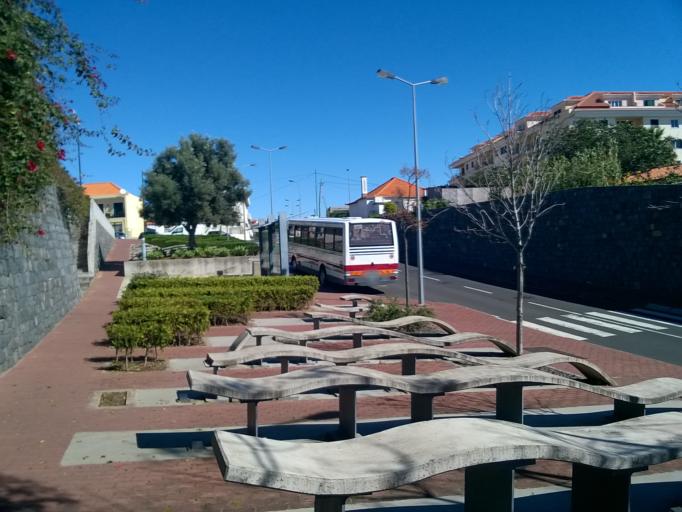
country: PT
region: Madeira
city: Canico
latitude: 32.6498
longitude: -16.8406
